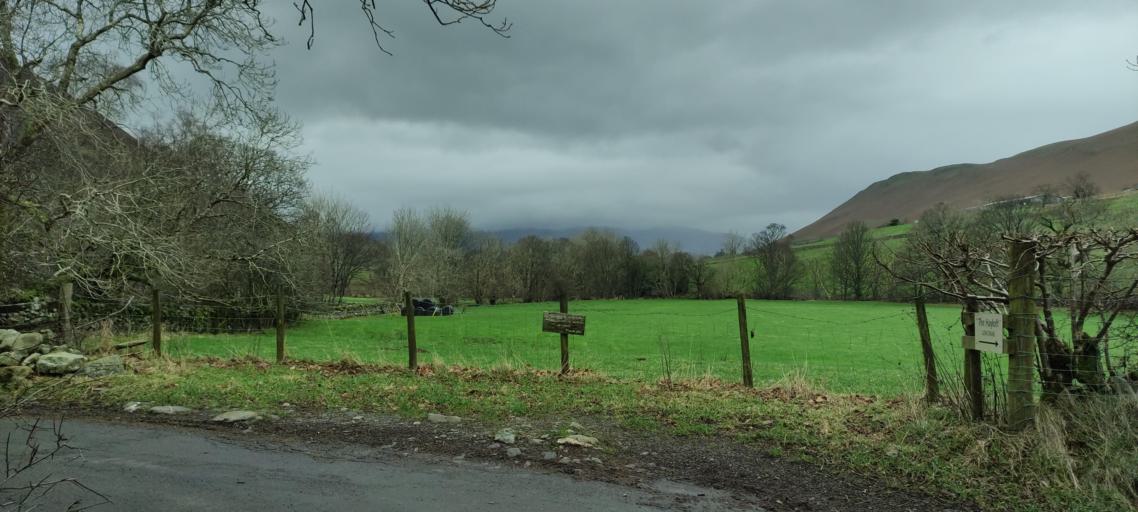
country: GB
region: England
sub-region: Cumbria
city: Keswick
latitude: 54.5641
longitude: -3.1908
